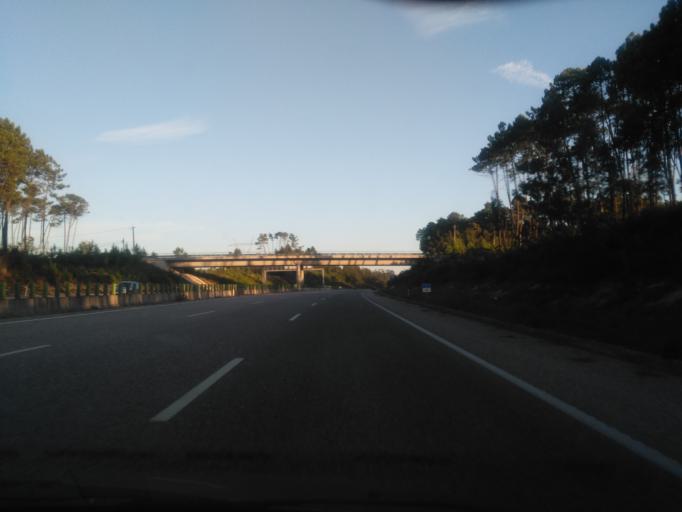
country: PT
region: Leiria
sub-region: Pombal
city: Lourical
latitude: 39.9656
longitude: -8.7778
